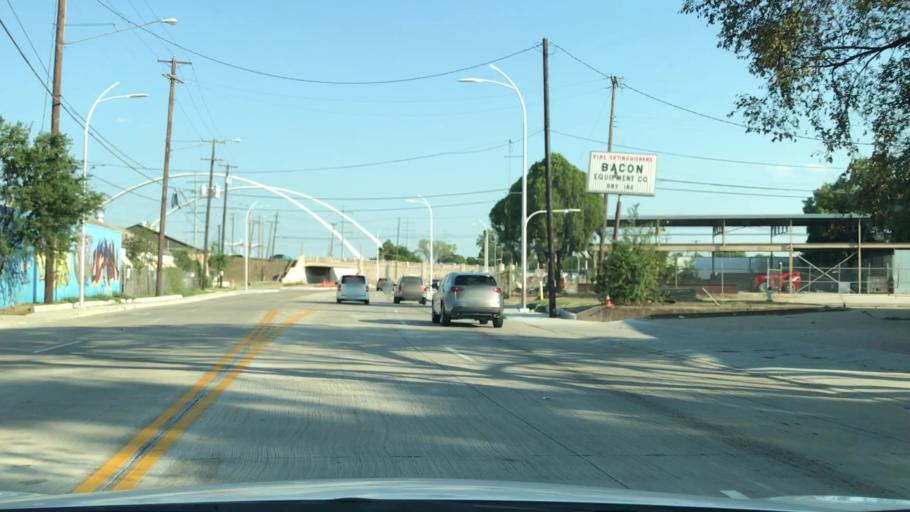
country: US
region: Texas
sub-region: Dallas County
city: Dallas
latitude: 32.7767
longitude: -96.8243
